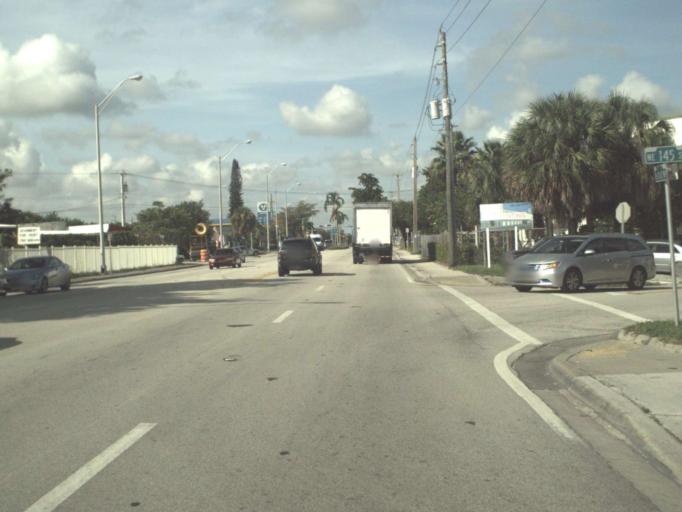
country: US
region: Florida
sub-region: Miami-Dade County
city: North Miami Beach
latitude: 25.9093
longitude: -80.1692
